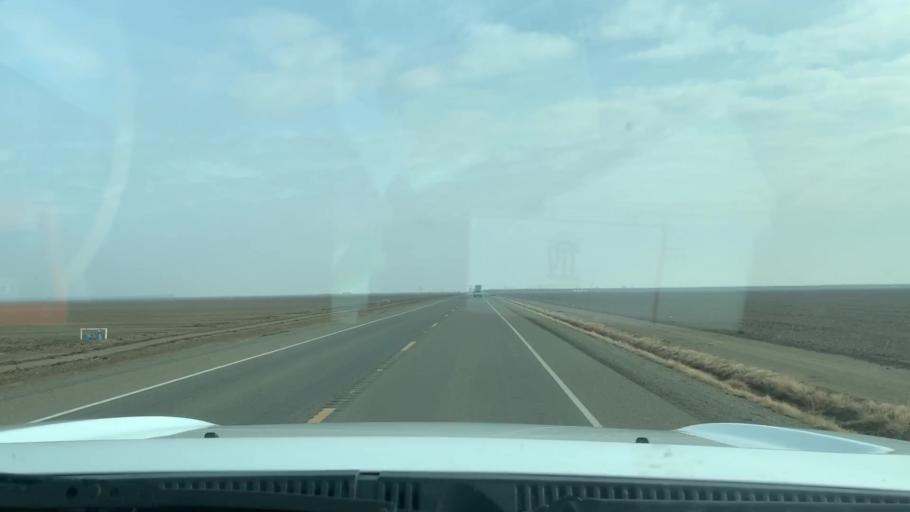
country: US
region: California
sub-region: Kings County
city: Lemoore Station
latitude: 36.2554
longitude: -119.9897
